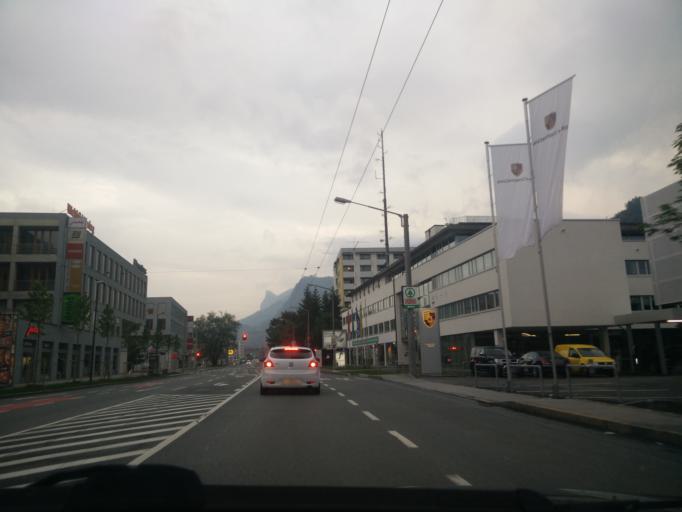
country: AT
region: Salzburg
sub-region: Salzburg Stadt
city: Salzburg
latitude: 47.8089
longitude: 13.0562
